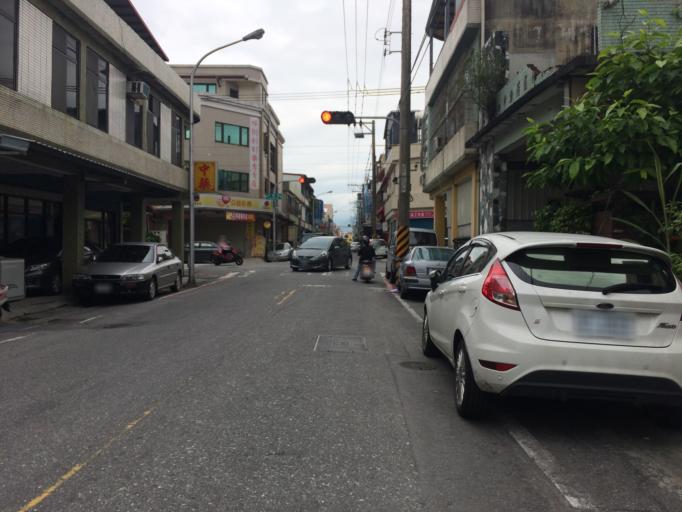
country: TW
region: Taiwan
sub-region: Hualien
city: Hualian
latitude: 23.9707
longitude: 121.6033
